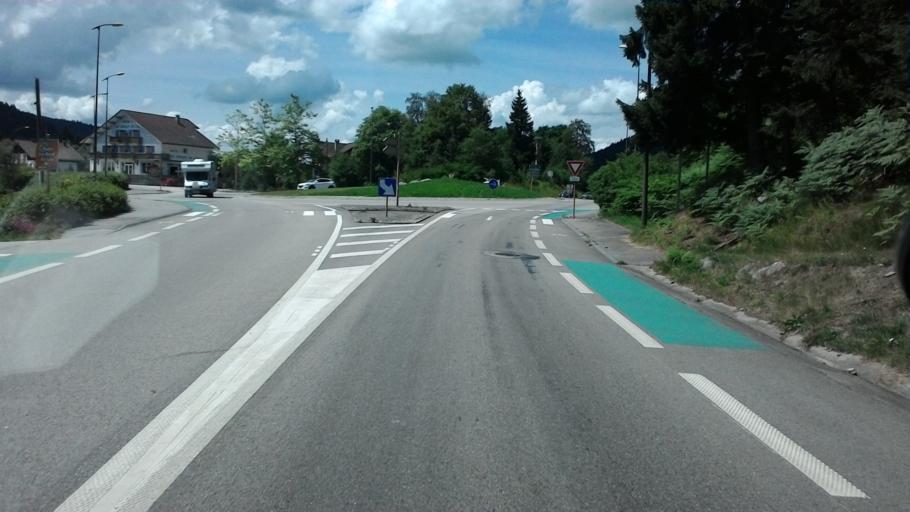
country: FR
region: Lorraine
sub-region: Departement des Vosges
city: Gerardmer
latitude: 48.0725
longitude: 6.8405
